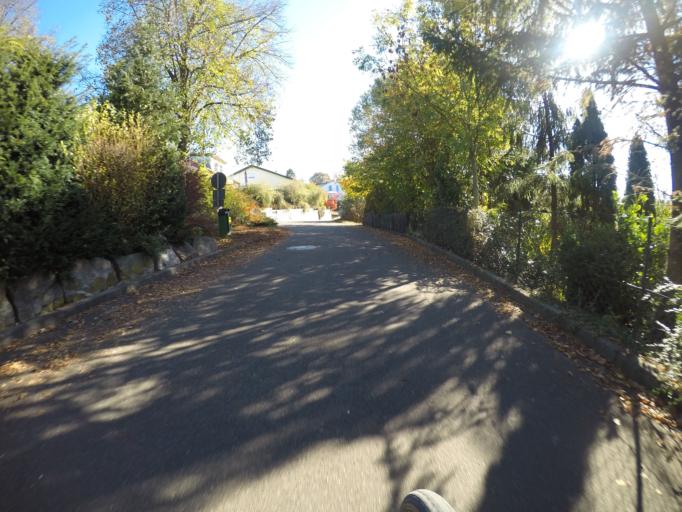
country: DE
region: Baden-Wuerttemberg
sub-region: Regierungsbezirk Stuttgart
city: Schlaitdorf
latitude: 48.6259
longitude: 9.2305
